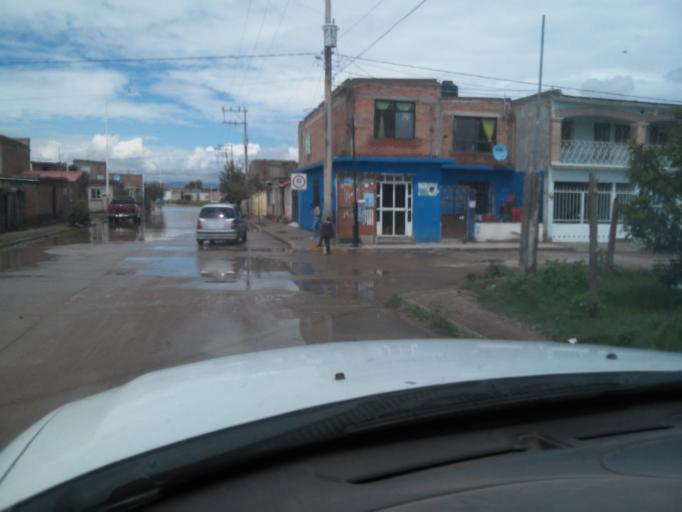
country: MX
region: Durango
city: Victoria de Durango
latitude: 24.0173
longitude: -104.6076
